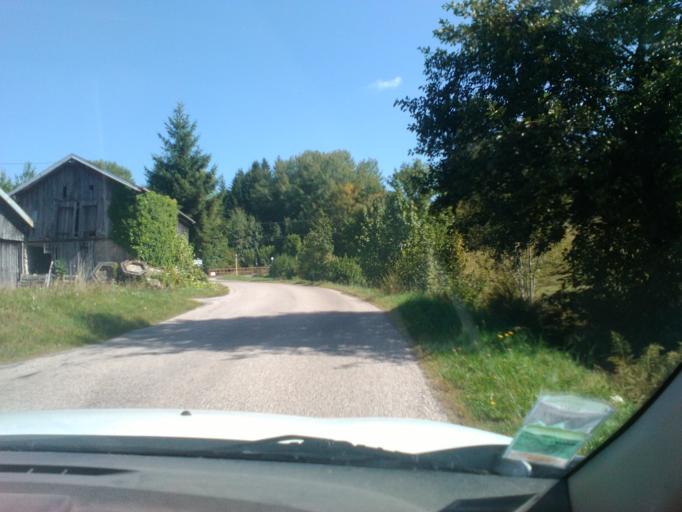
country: FR
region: Lorraine
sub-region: Departement des Vosges
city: Granges-sur-Vologne
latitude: 48.0924
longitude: 6.8073
